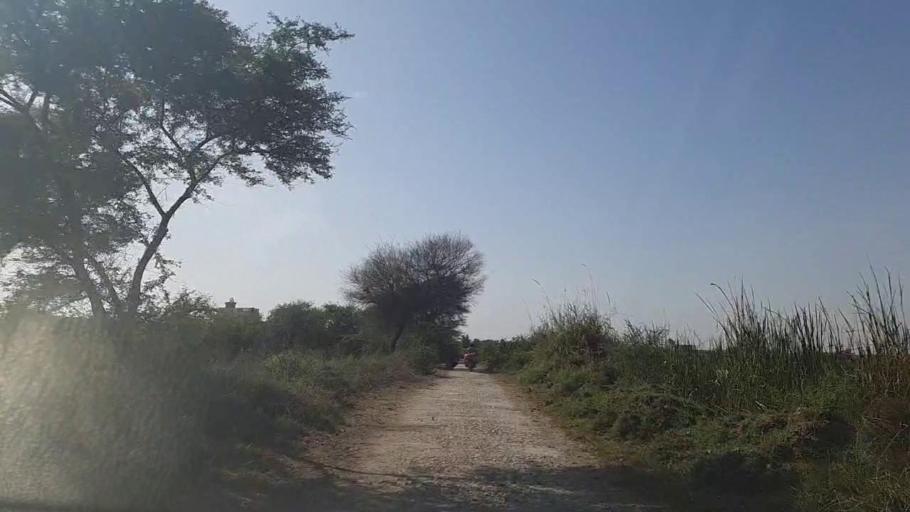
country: PK
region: Sindh
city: Thatta
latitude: 24.5911
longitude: 67.8896
